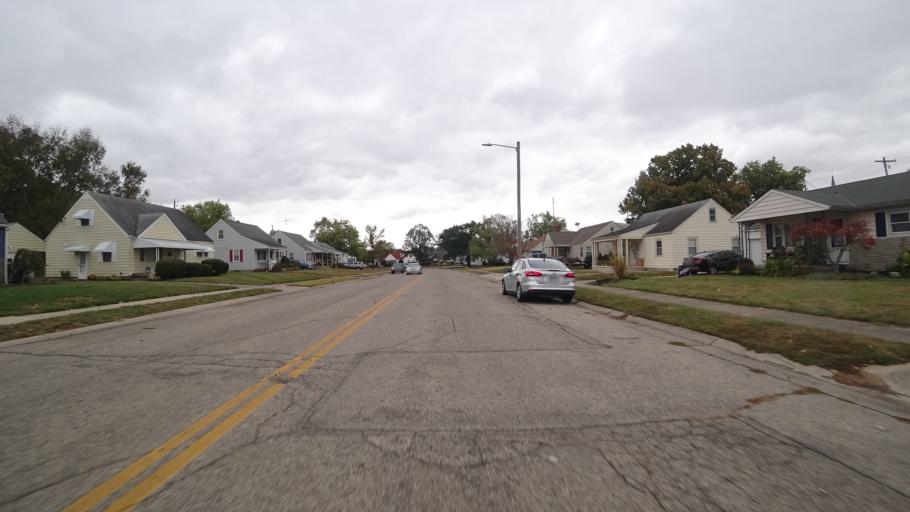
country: US
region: Ohio
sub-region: Butler County
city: Fairfield
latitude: 39.3610
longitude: -84.5604
